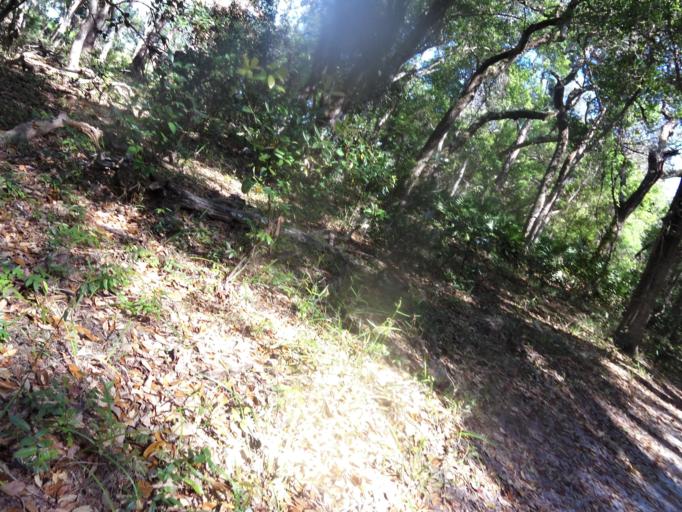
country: US
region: Florida
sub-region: Saint Johns County
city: Villano Beach
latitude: 29.9988
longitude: -81.3277
